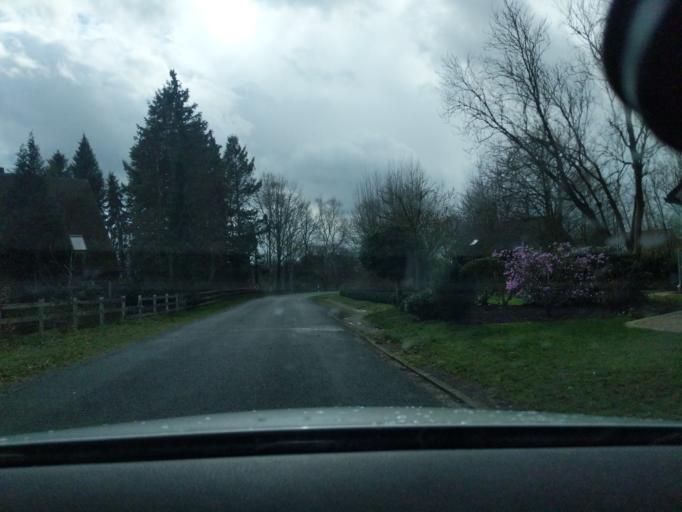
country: DE
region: Lower Saxony
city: Kranenburg
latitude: 53.6013
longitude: 9.2056
